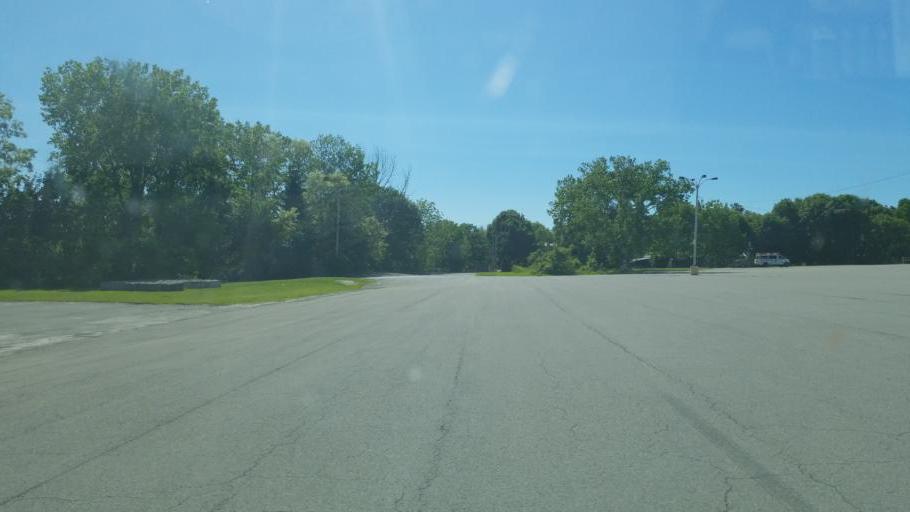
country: US
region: New York
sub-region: Montgomery County
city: Canajoharie
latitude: 42.9123
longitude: -74.5716
